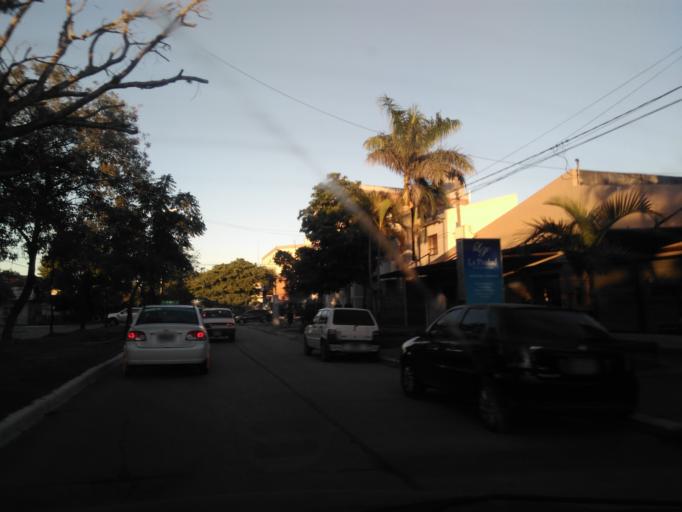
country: AR
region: Chaco
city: Resistencia
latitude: -27.4617
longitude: -58.9897
